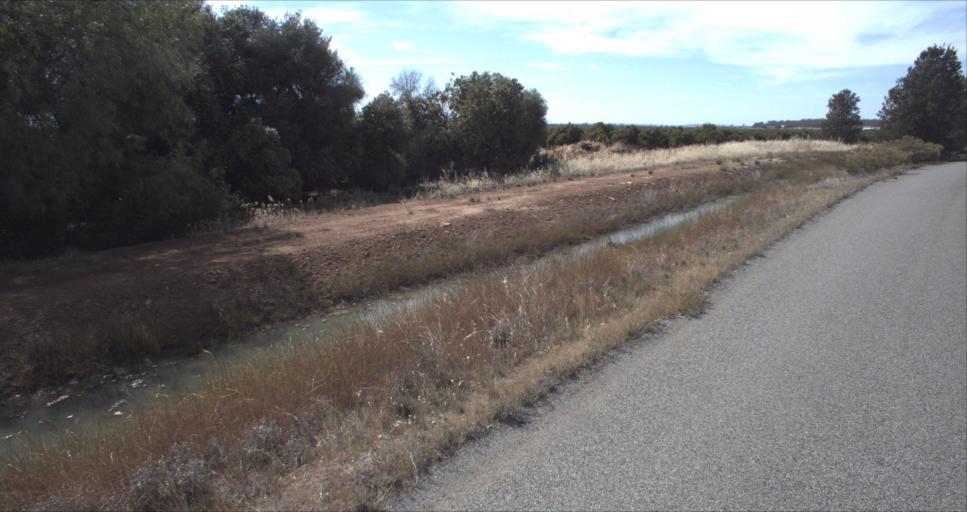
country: AU
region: New South Wales
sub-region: Leeton
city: Leeton
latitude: -34.5842
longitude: 146.4612
